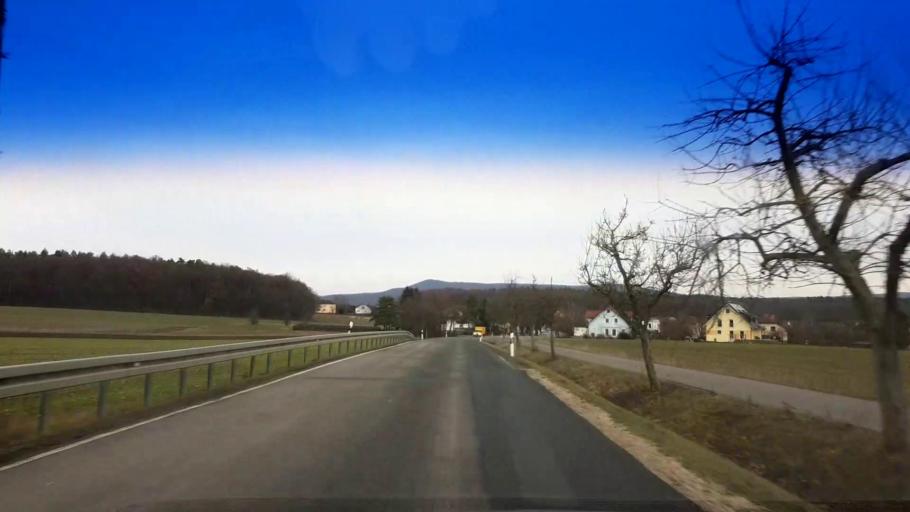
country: DE
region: Bavaria
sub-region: Upper Franconia
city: Memmelsdorf
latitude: 49.9327
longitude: 10.9737
